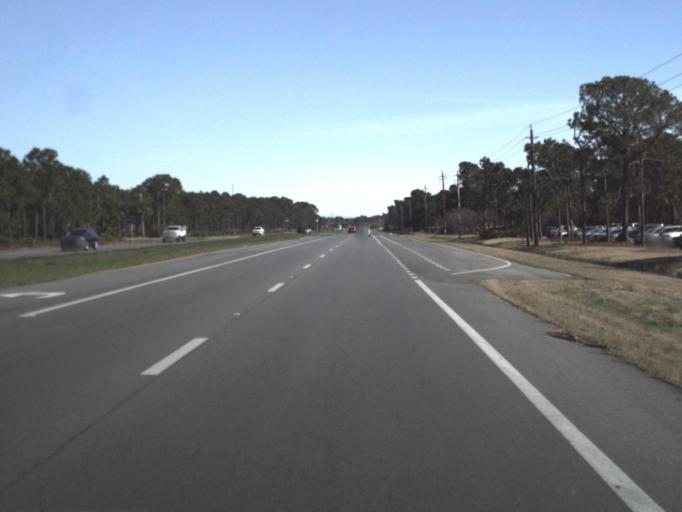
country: US
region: Florida
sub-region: Bay County
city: Panama City Beach
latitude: 30.1932
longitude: -85.8023
